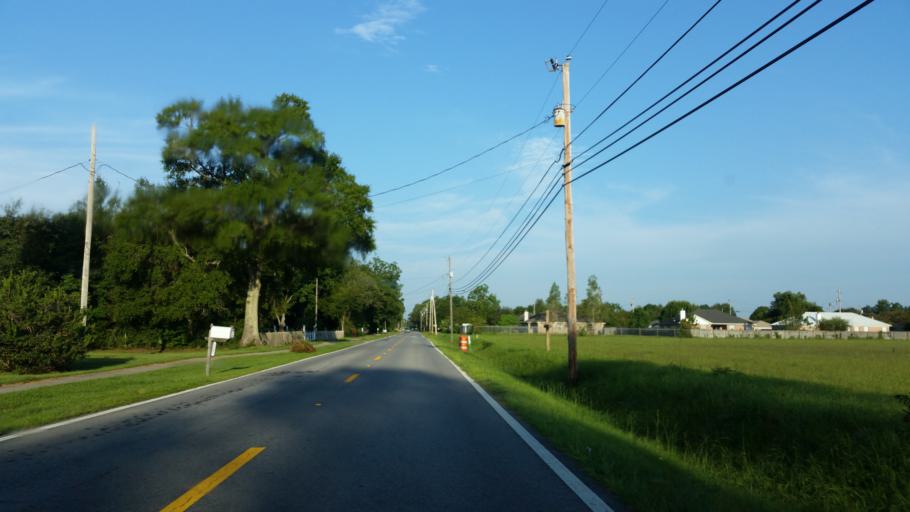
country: US
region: Florida
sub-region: Escambia County
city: Bellview
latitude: 30.4688
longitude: -87.3163
